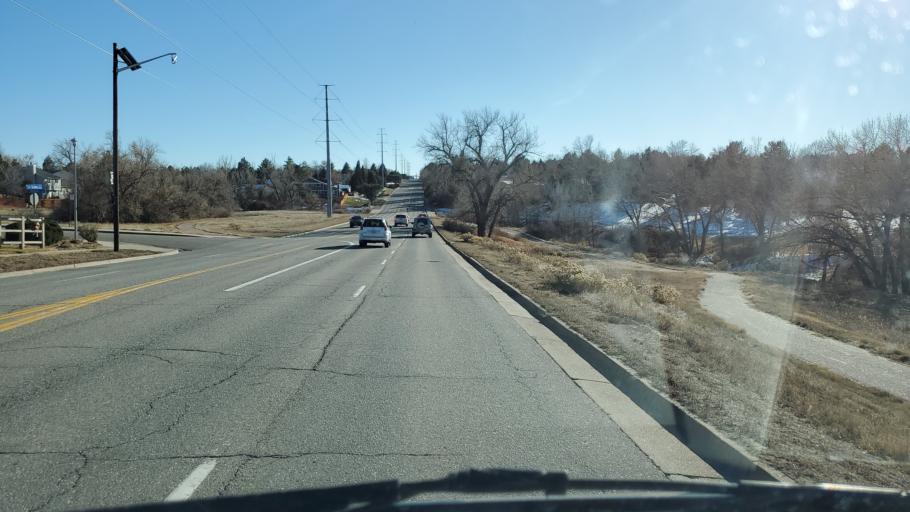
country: US
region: Colorado
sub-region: Arapahoe County
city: Castlewood
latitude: 39.5785
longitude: -104.9044
